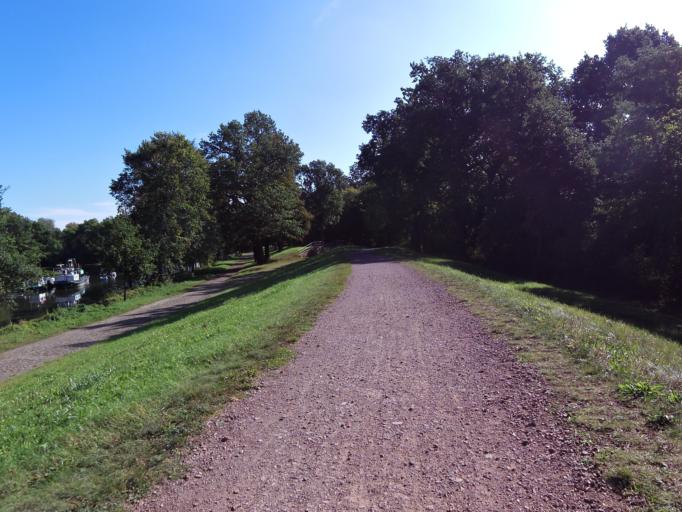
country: DE
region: Saxony-Anhalt
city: Dessau
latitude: 51.8551
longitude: 12.2214
